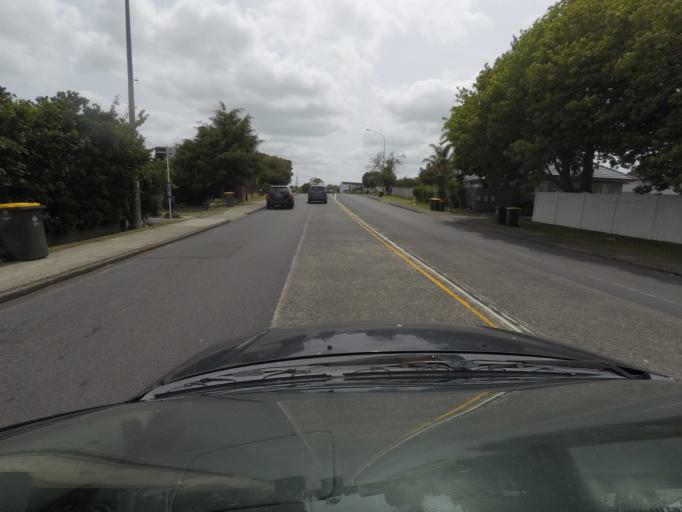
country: NZ
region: Auckland
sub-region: Auckland
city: Pakuranga
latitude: -36.8976
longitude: 174.9207
